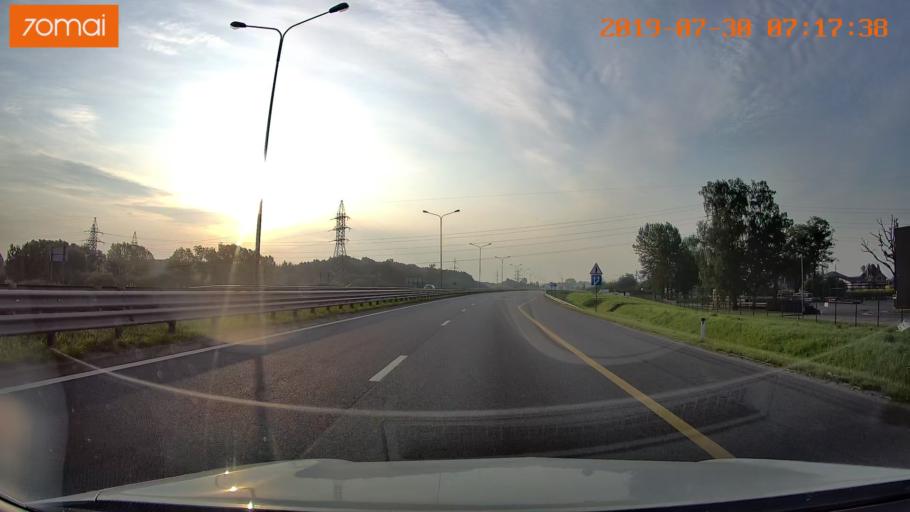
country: RU
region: Kaliningrad
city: Bol'shoe Isakovo
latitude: 54.7068
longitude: 20.6315
